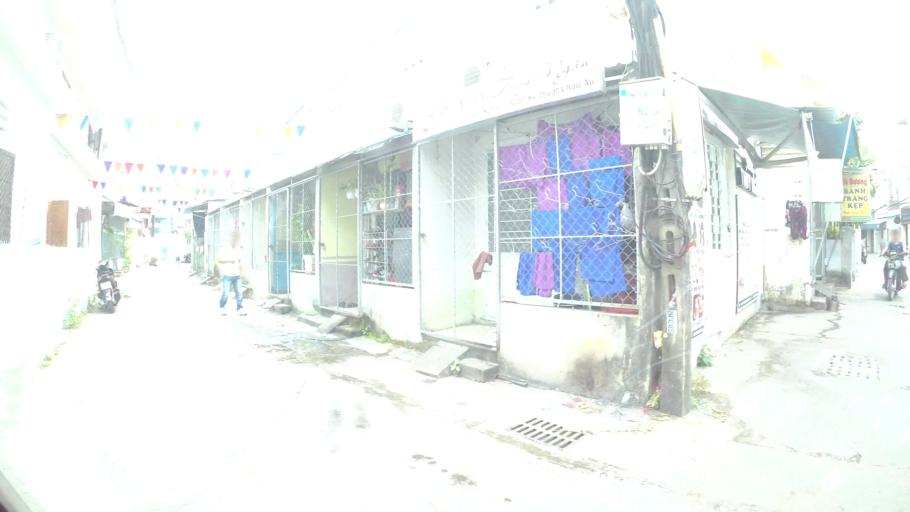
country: VN
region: Da Nang
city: Thanh Khe
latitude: 16.0675
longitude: 108.1987
